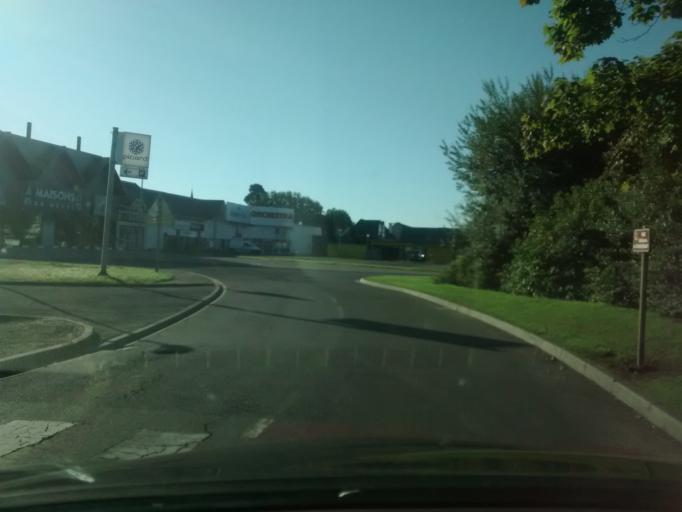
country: FR
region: Lower Normandy
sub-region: Departement du Calvados
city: Touques
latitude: 49.3471
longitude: 0.0978
